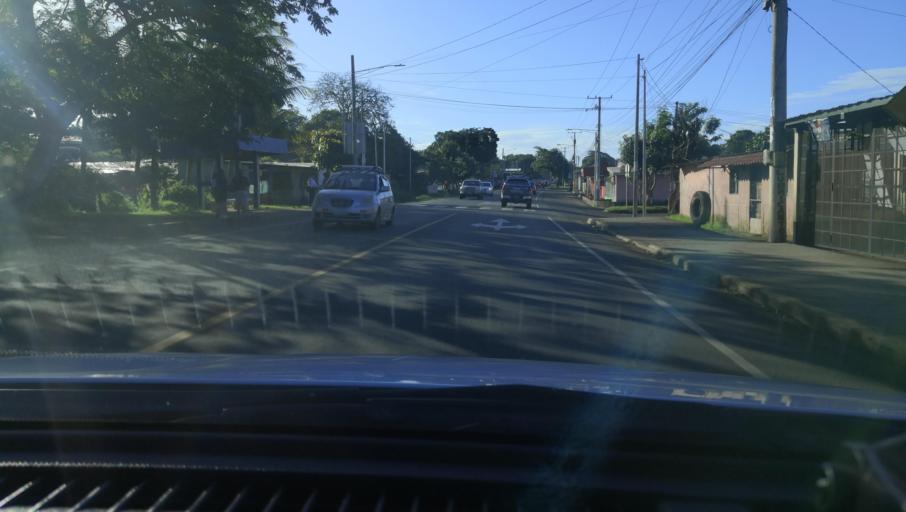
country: NI
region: Carazo
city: Dolores
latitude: 11.8586
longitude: -86.2163
